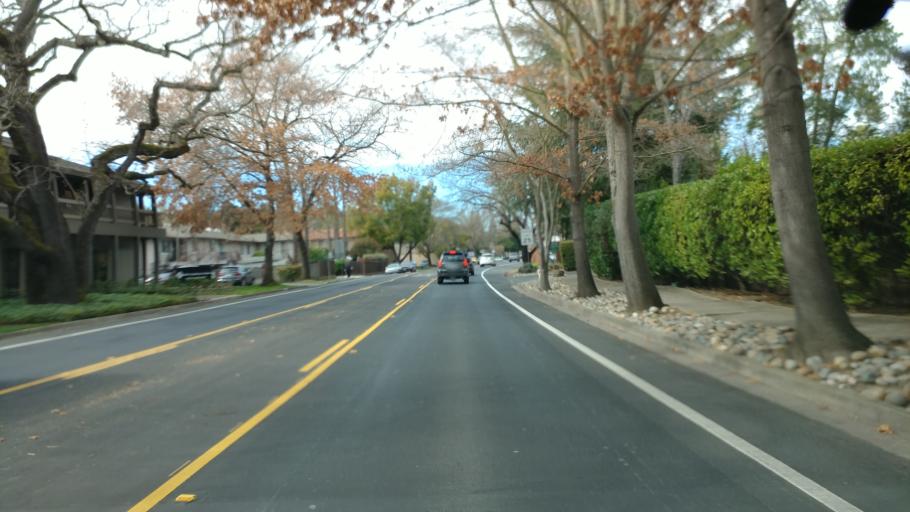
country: US
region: California
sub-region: Contra Costa County
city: Alamo
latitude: 37.8459
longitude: -122.0295
